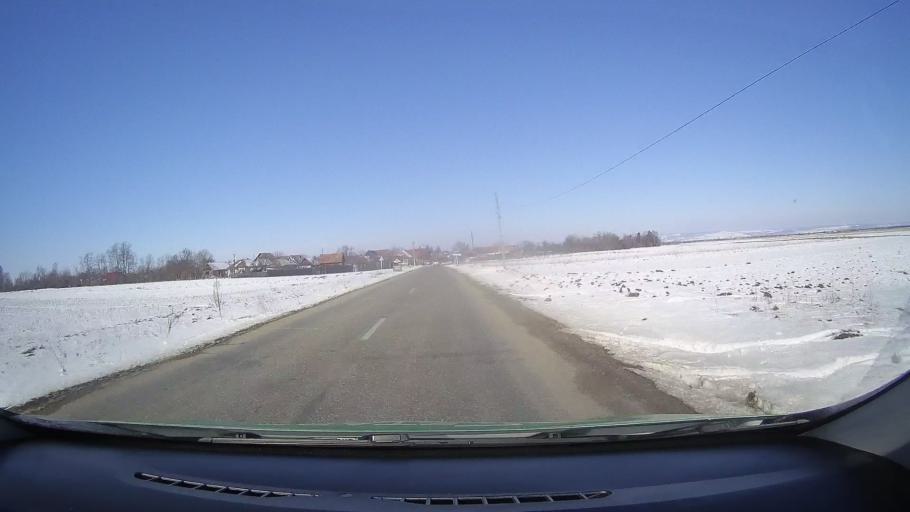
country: RO
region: Brasov
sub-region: Comuna Harseni
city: Harseni
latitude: 45.7489
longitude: 25.0156
